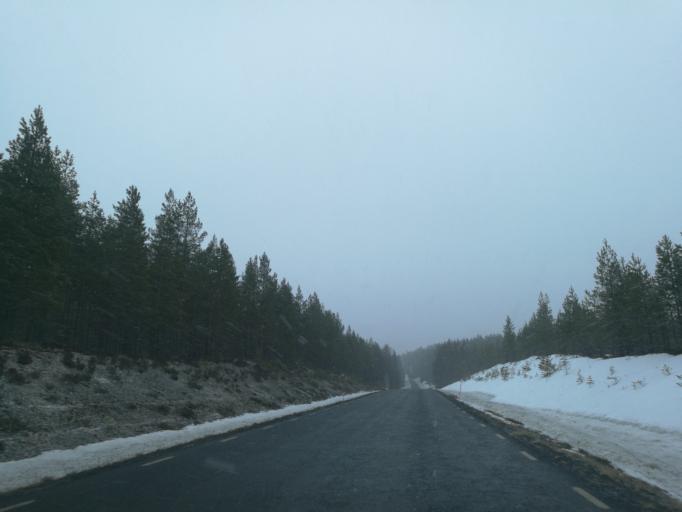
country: SE
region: Vaermland
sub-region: Torsby Kommun
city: Torsby
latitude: 60.6754
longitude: 12.6856
